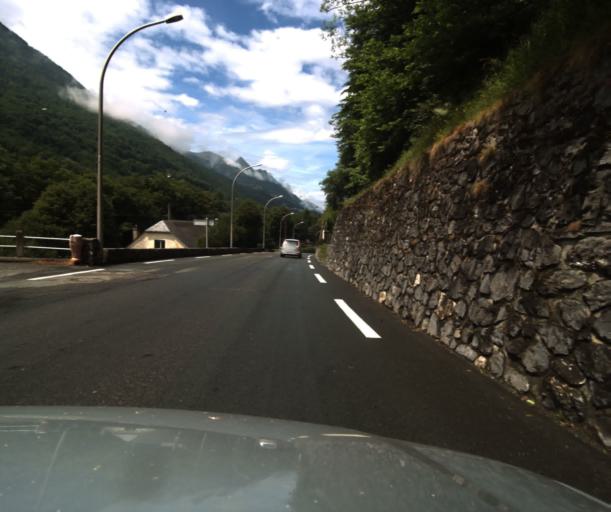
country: FR
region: Midi-Pyrenees
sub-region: Departement des Hautes-Pyrenees
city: Luz-Saint-Sauveur
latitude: 42.8637
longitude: -0.0078
